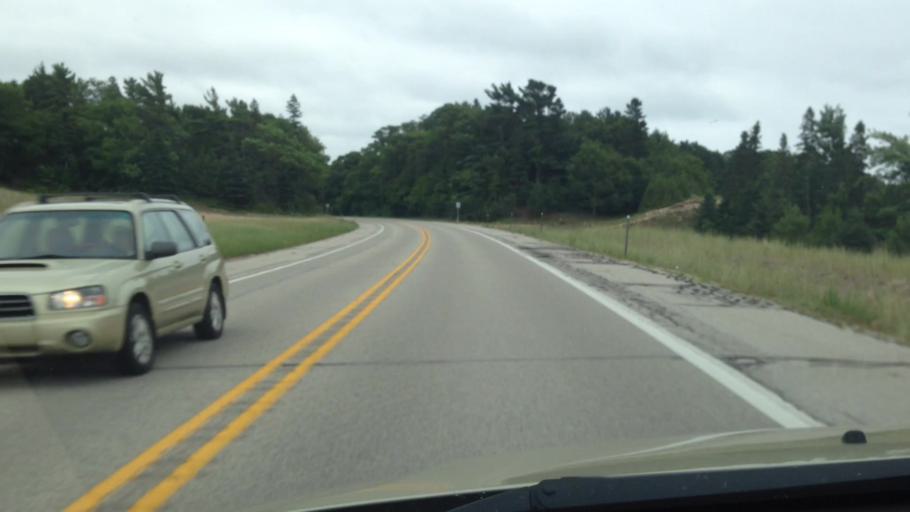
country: US
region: Michigan
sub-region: Mackinac County
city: Saint Ignace
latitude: 45.9316
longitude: -84.9166
